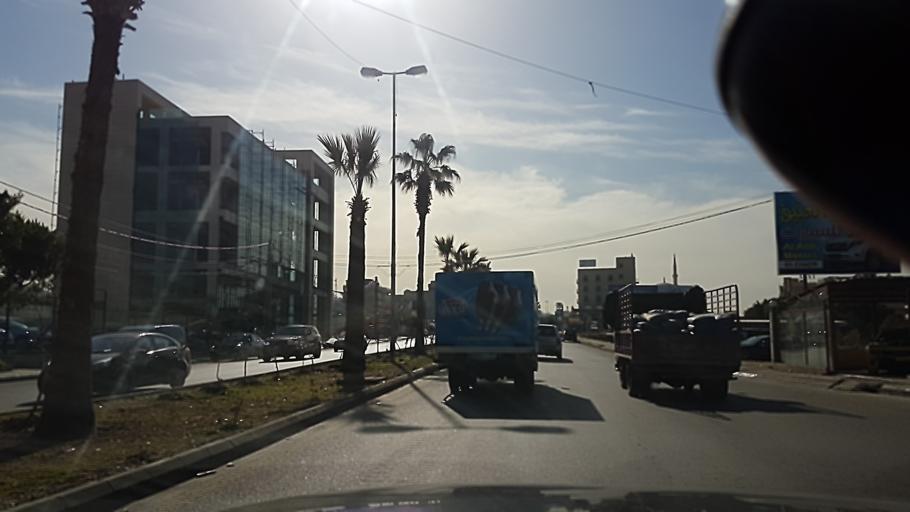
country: LB
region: Liban-Sud
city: Sidon
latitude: 33.5832
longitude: 35.3864
